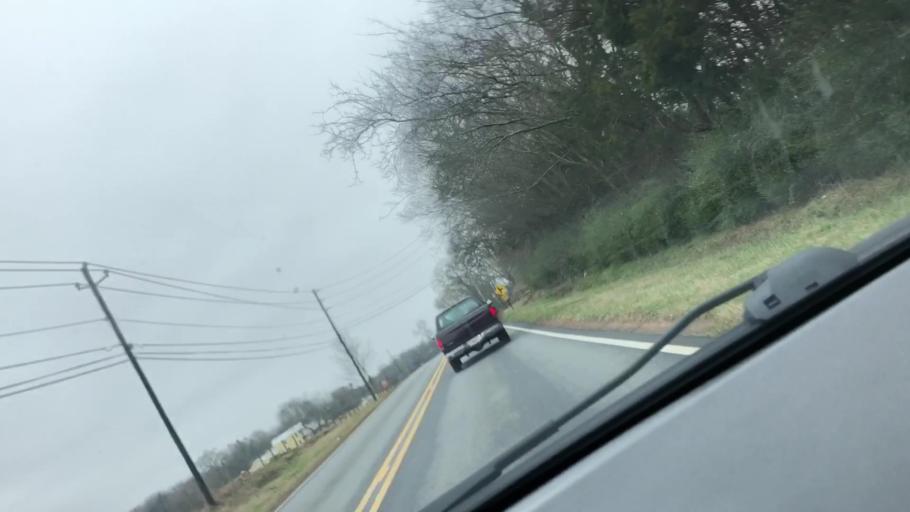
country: US
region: Georgia
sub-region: Bartow County
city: Cartersville
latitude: 34.1955
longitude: -84.8356
